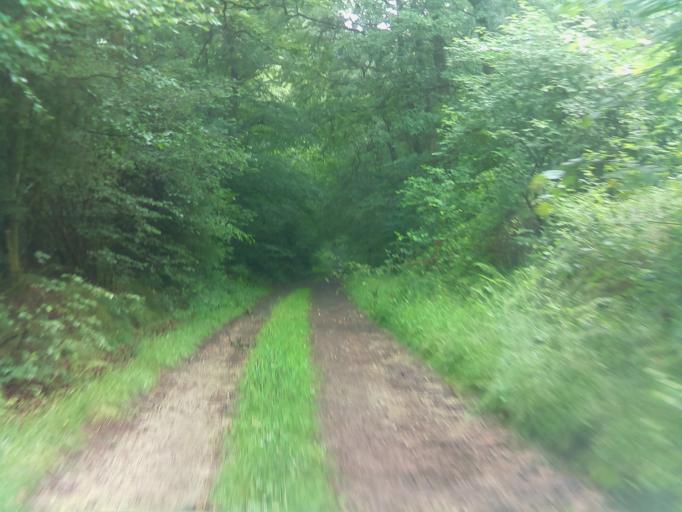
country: BE
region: Wallonia
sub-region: Province de Namur
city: Bievre
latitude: 49.9824
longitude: 5.0113
